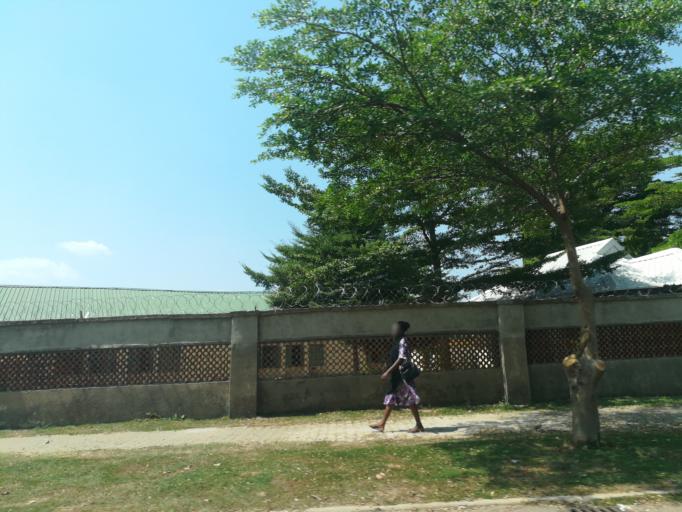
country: NG
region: Abuja Federal Capital Territory
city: Abuja
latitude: 9.0667
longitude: 7.4271
